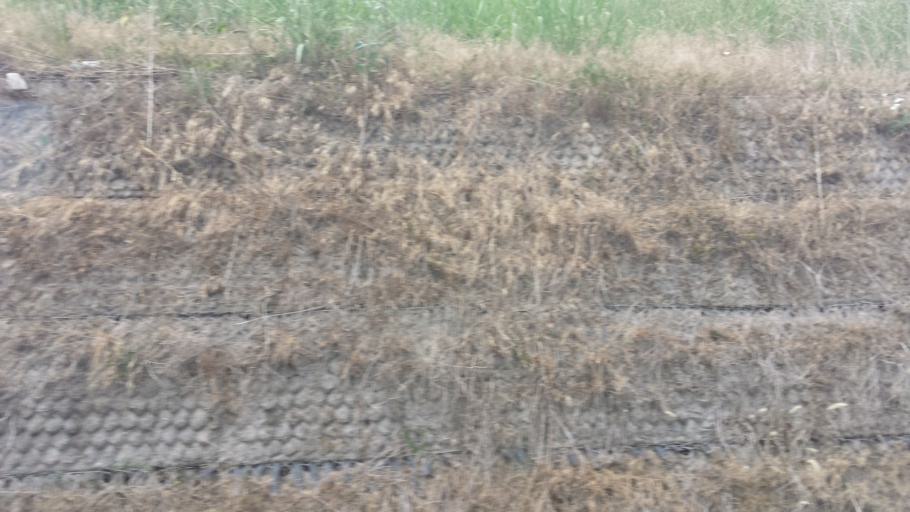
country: RO
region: Constanta
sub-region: Comuna Ovidiu
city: Ovidiu
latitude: 44.2620
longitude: 28.5533
